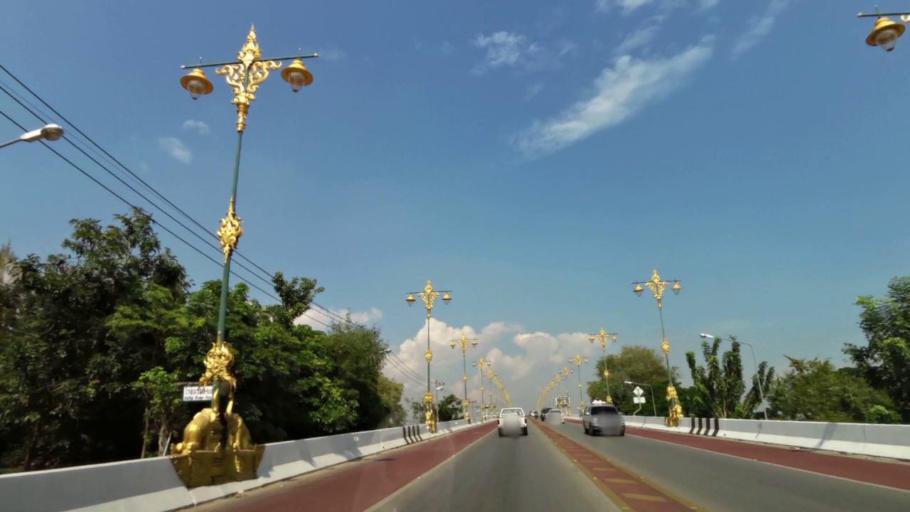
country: TH
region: Chiang Rai
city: Chiang Rai
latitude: 19.9161
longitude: 99.8325
